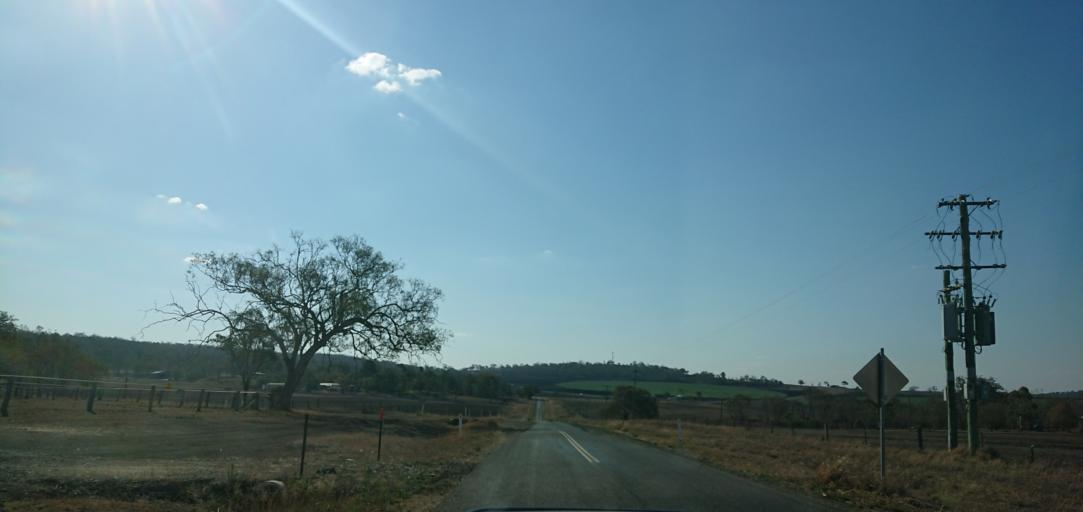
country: AU
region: Queensland
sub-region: Toowoomba
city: Westbrook
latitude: -27.7163
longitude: 151.7200
